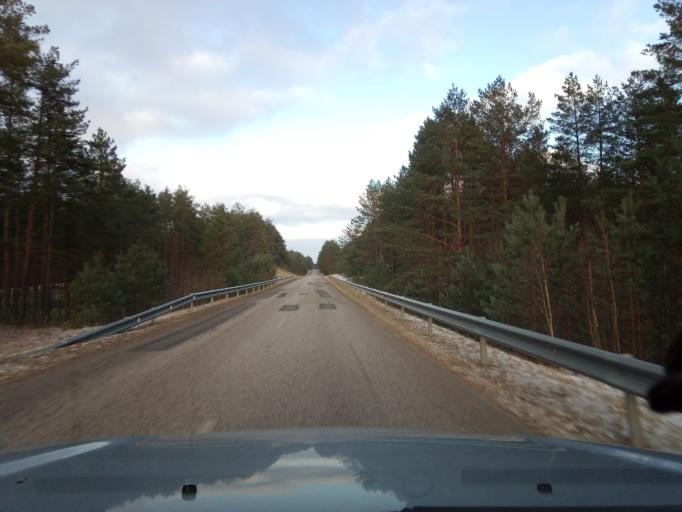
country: LT
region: Alytaus apskritis
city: Varena
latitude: 54.1111
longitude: 24.4400
